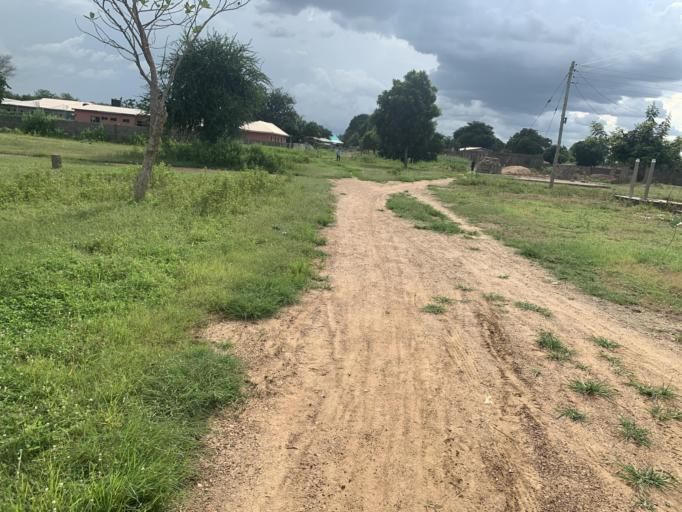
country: GH
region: Upper East
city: Navrongo
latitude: 10.8706
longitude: -1.0729
